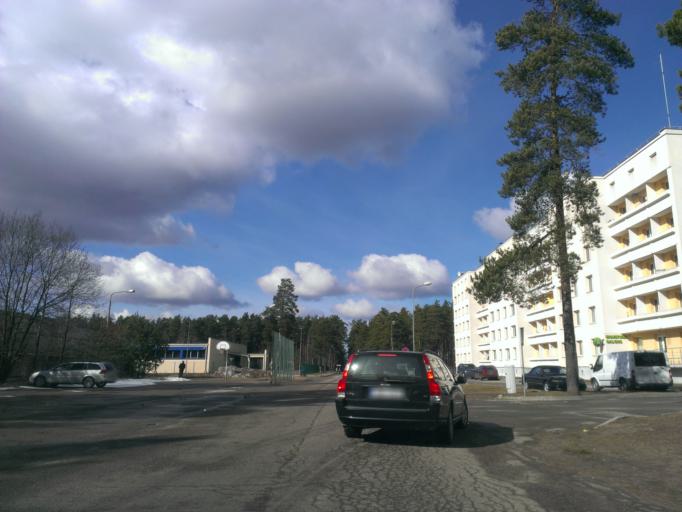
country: LV
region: Garkalne
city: Garkalne
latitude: 56.9643
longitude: 24.4285
